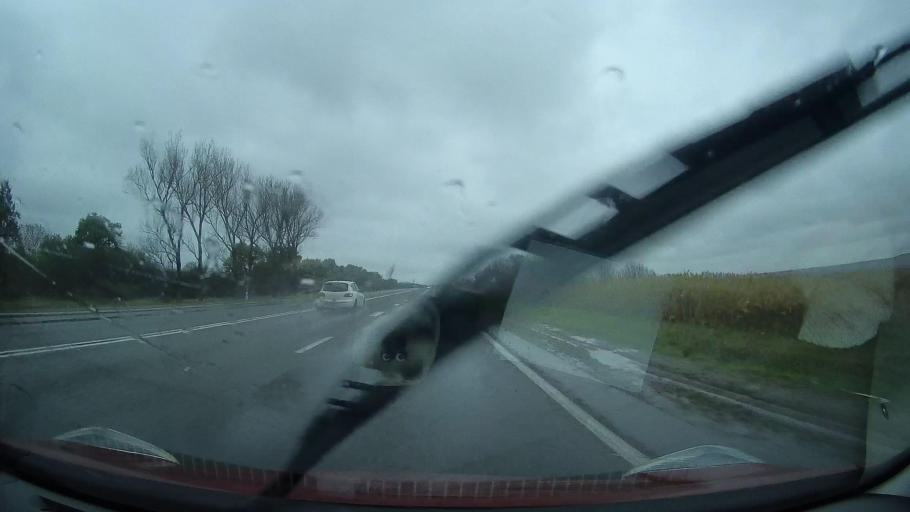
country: RU
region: Stavropol'skiy
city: Nevinnomyssk
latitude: 44.6311
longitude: 42.0258
